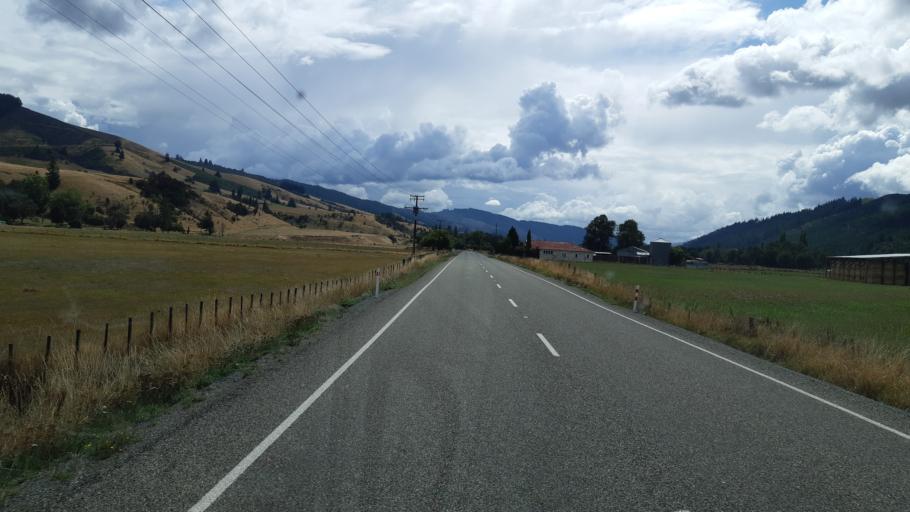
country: NZ
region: Tasman
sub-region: Tasman District
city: Wakefield
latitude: -41.5168
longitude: 172.7956
